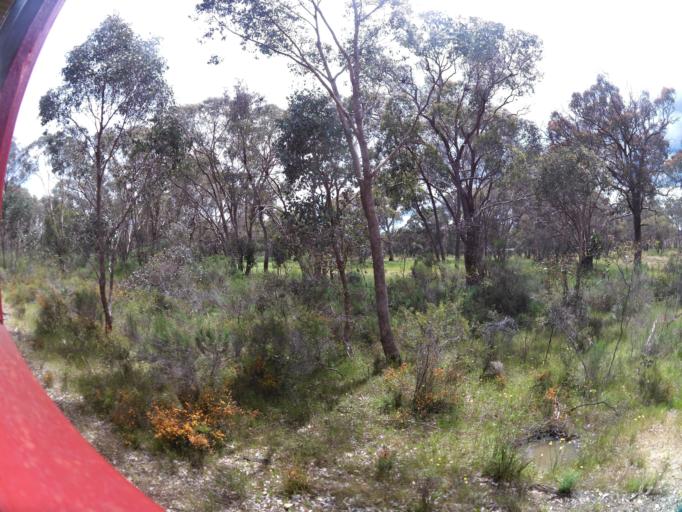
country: AU
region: Victoria
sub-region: Mount Alexander
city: Castlemaine
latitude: -36.9924
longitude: 144.0925
